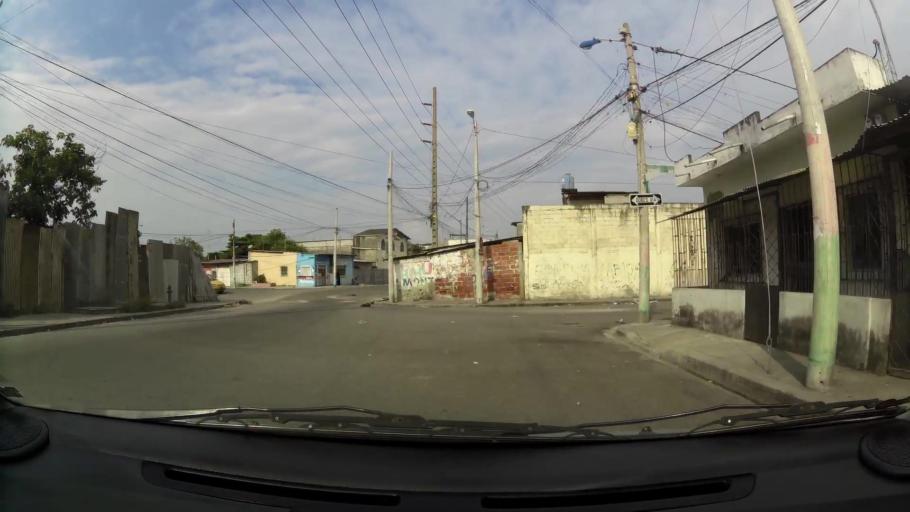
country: EC
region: Guayas
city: Guayaquil
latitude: -2.2488
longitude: -79.9070
